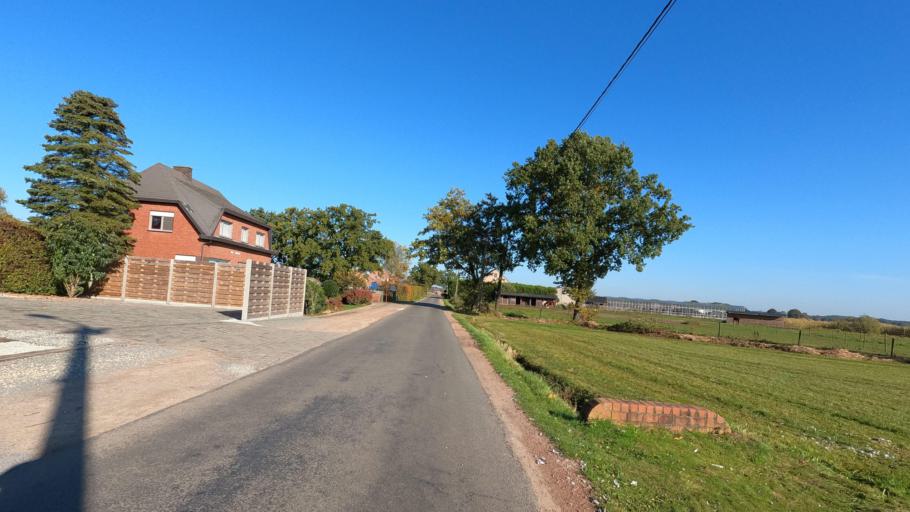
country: BE
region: Flanders
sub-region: Provincie Antwerpen
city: Oostmalle
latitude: 51.3126
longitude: 4.7485
